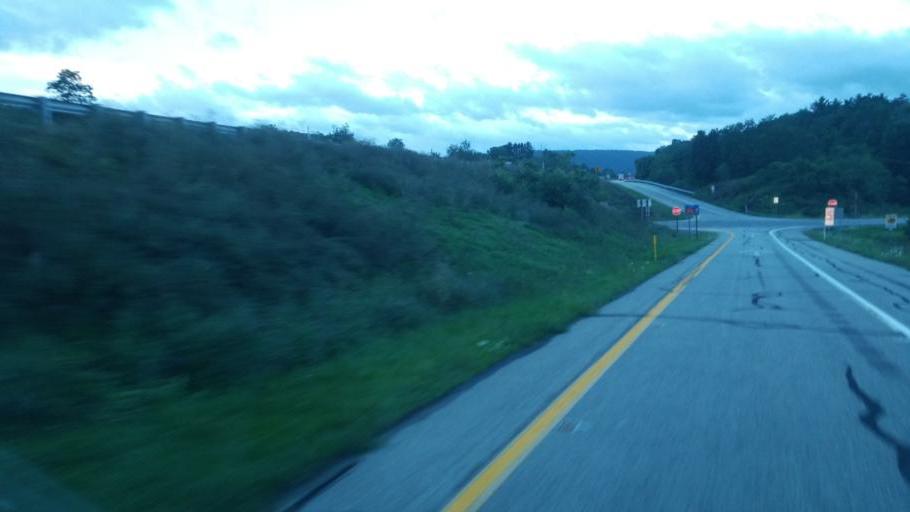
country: US
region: Pennsylvania
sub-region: Bedford County
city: Earlston
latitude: 39.9798
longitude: -78.2450
